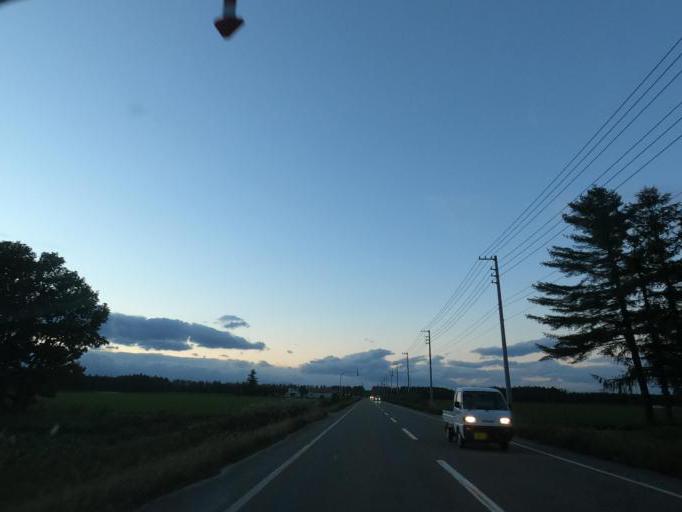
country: JP
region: Hokkaido
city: Obihiro
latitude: 42.6671
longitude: 143.1747
